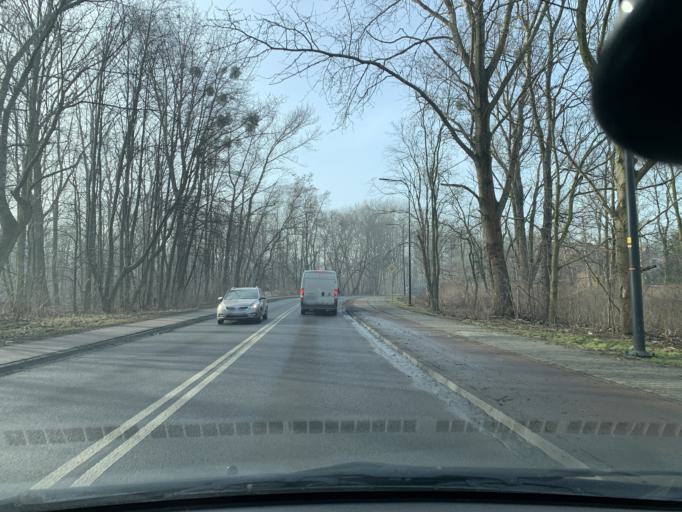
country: PL
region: Silesian Voivodeship
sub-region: Swietochlowice
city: Swietochlowice
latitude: 50.3279
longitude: 18.8622
